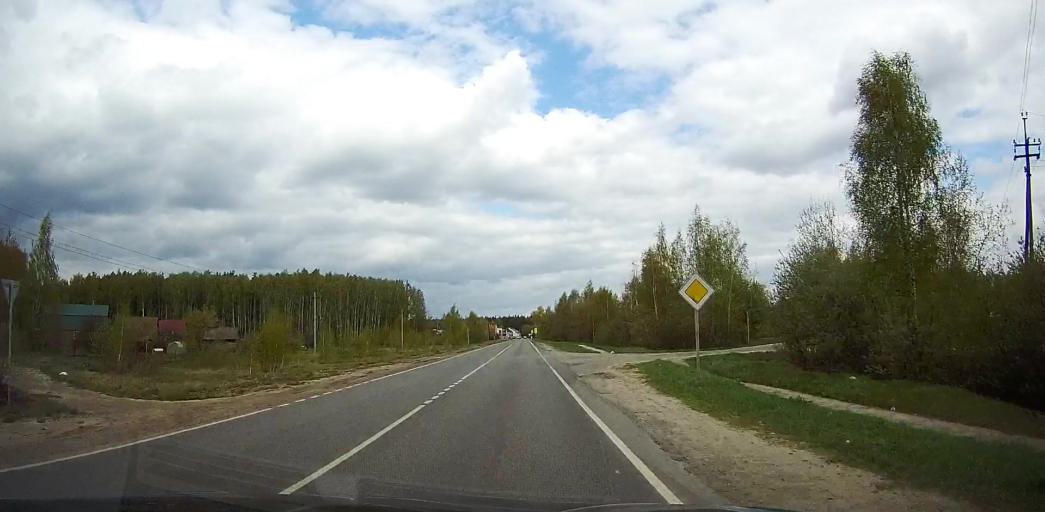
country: RU
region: Moskovskaya
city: Ashitkovo
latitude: 55.4329
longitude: 38.5784
